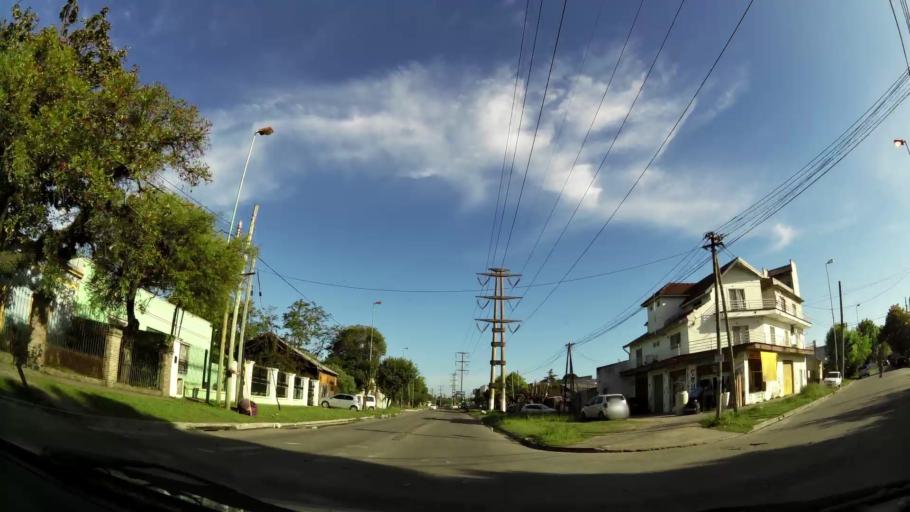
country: AR
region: Buenos Aires
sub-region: Partido de Quilmes
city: Quilmes
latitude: -34.8045
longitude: -58.2163
